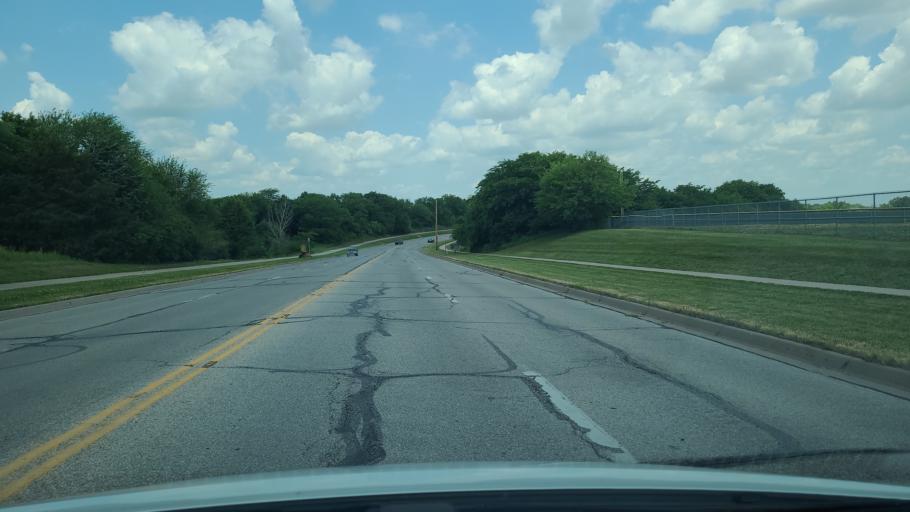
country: US
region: Kansas
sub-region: Douglas County
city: Lawrence
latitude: 38.9753
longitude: -95.3081
